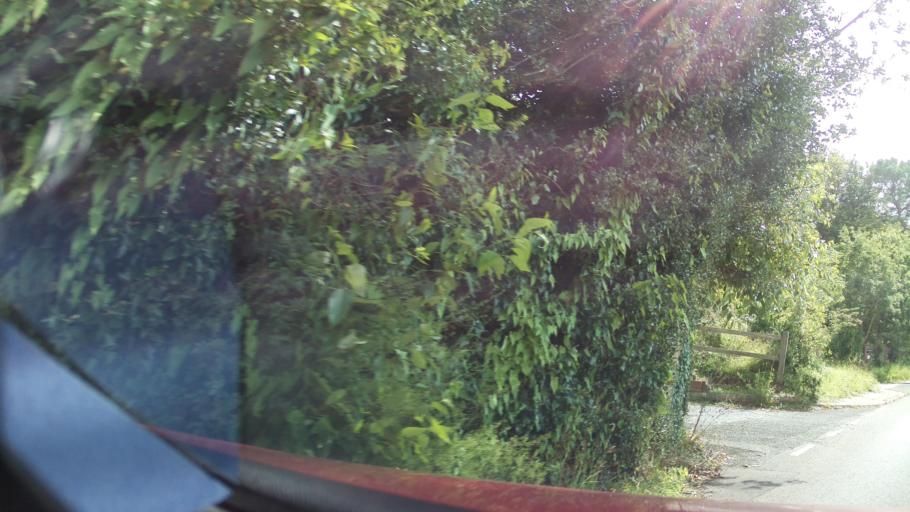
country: GB
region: England
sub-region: Borough of Torbay
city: Torquay
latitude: 50.5057
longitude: -3.5254
